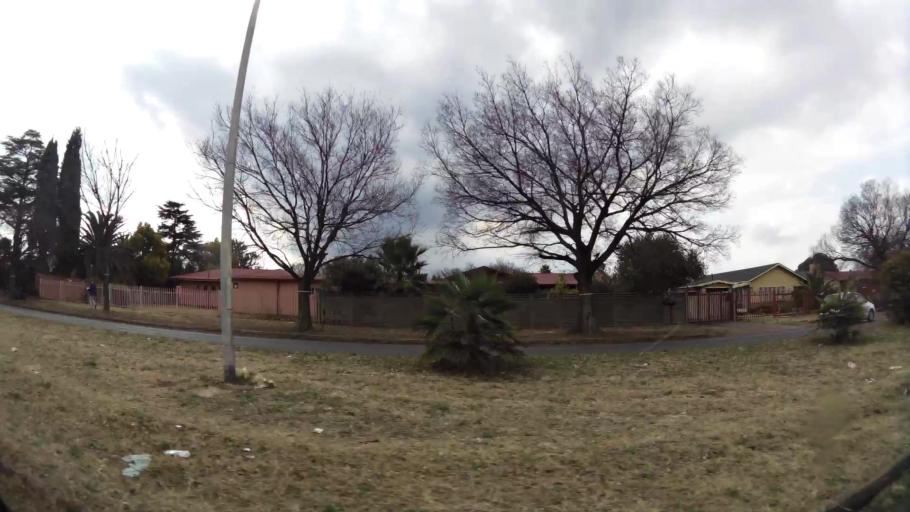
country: ZA
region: Gauteng
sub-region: Sedibeng District Municipality
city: Vanderbijlpark
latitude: -26.7218
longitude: 27.8307
